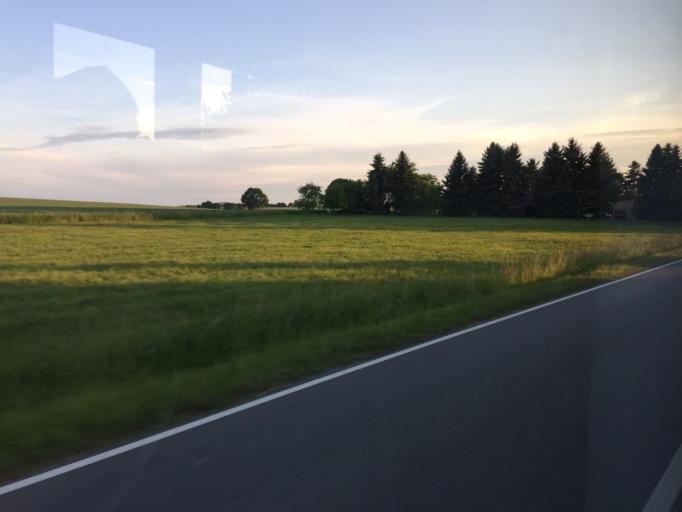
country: DE
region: Saxony
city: Markersdorf
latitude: 51.1480
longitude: 14.9023
